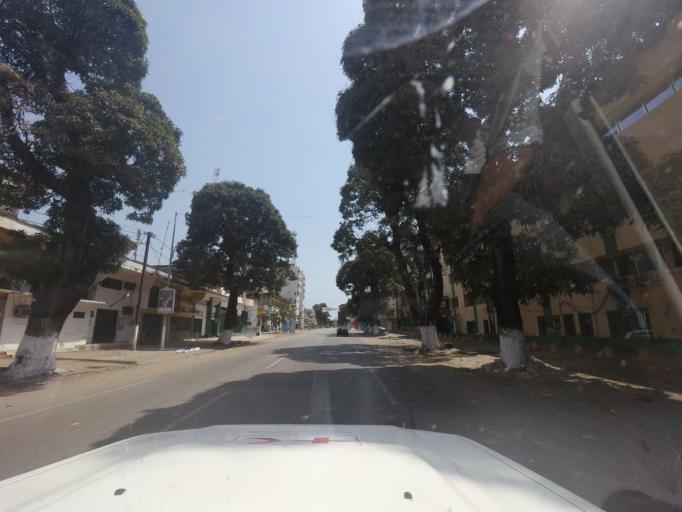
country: GN
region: Conakry
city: Camayenne
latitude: 9.5130
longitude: -13.7143
